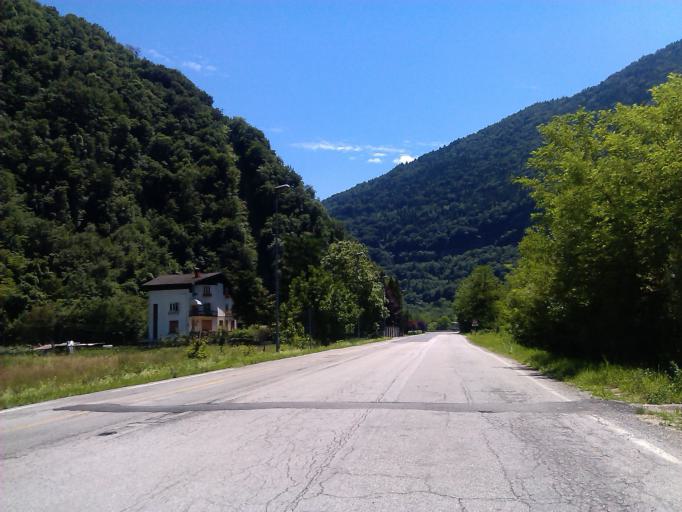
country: IT
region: Veneto
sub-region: Provincia di Vicenza
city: Enego
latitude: 45.9629
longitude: 11.7085
